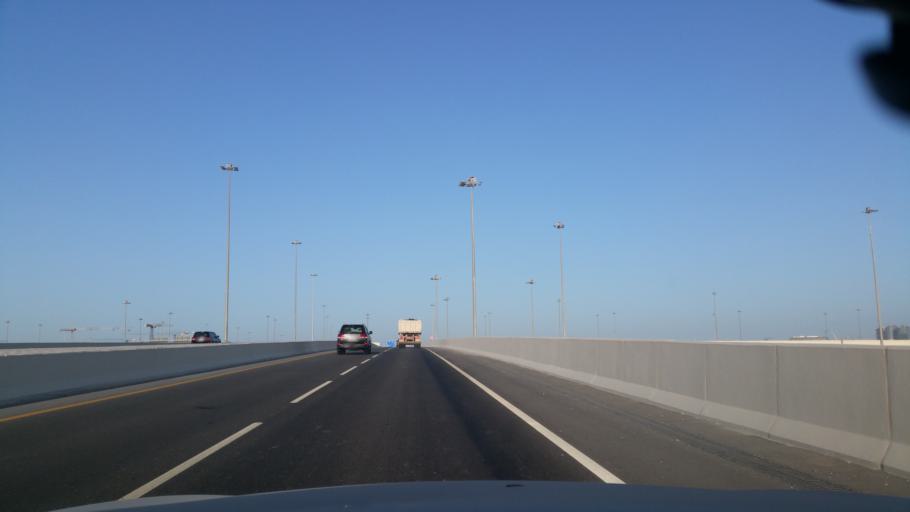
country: QA
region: Baladiyat Umm Salal
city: Umm Salal Muhammad
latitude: 25.4024
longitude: 51.4879
